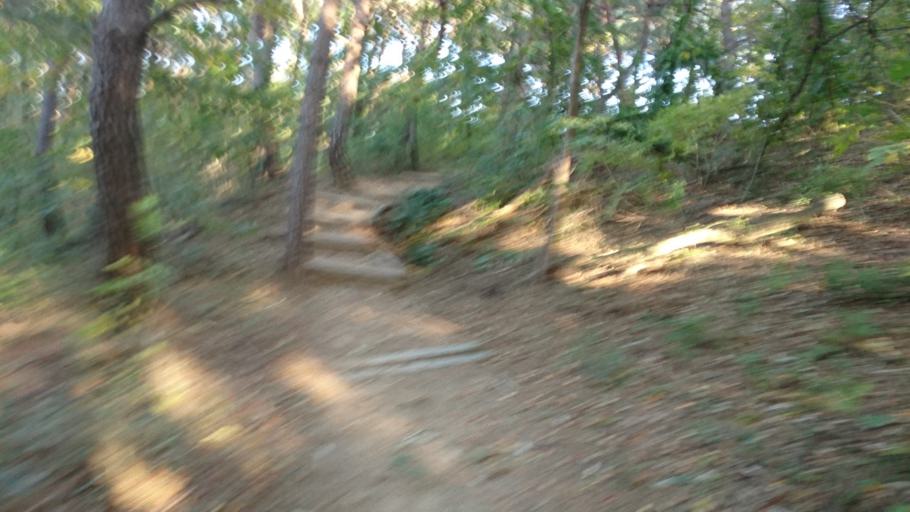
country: KR
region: Gyeongsangbuk-do
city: Kyonju
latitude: 35.8168
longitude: 129.2269
